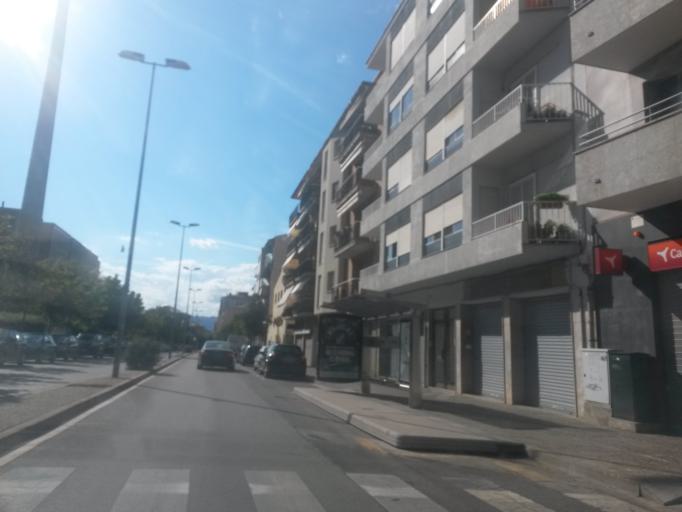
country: ES
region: Catalonia
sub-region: Provincia de Girona
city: Girona
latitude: 41.9684
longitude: 2.8211
